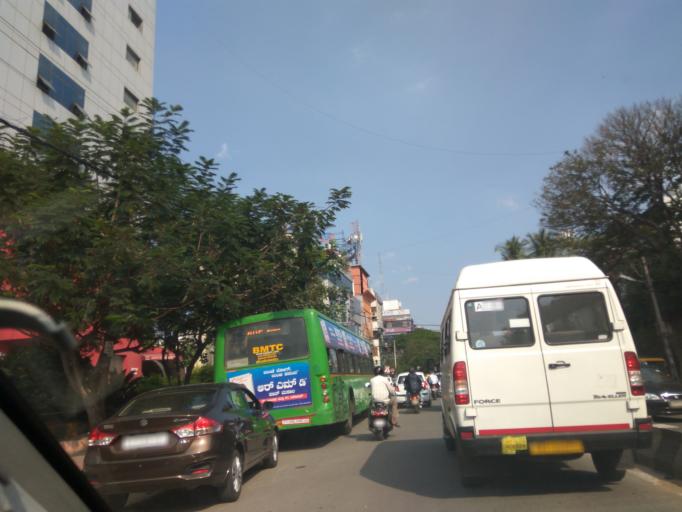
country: IN
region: Karnataka
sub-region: Bangalore Urban
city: Bangalore
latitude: 12.9407
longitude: 77.6246
